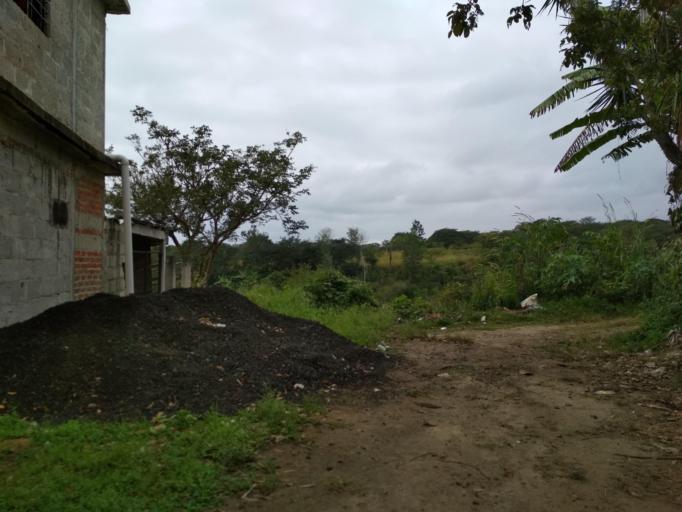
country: MX
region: Veracruz
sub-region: Emiliano Zapata
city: Dos Rios
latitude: 19.5212
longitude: -96.7958
